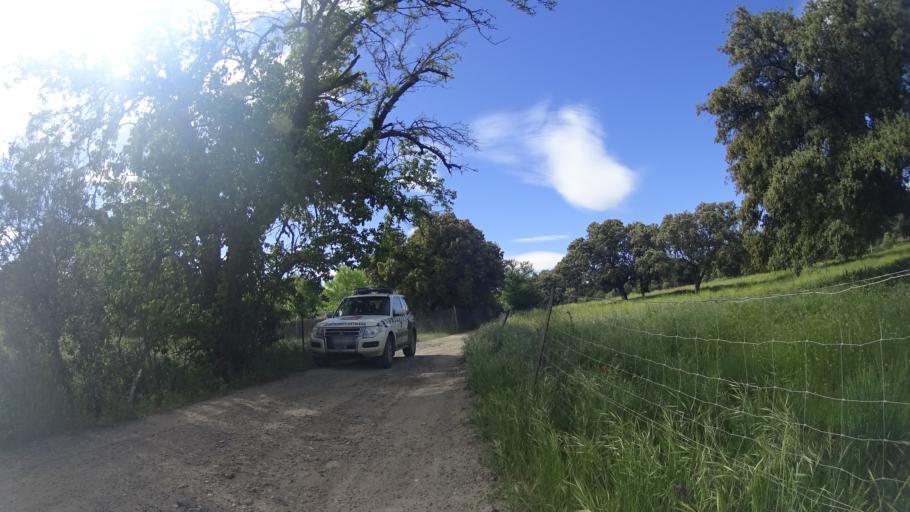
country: ES
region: Madrid
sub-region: Provincia de Madrid
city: Brunete
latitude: 40.4222
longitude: -3.9497
